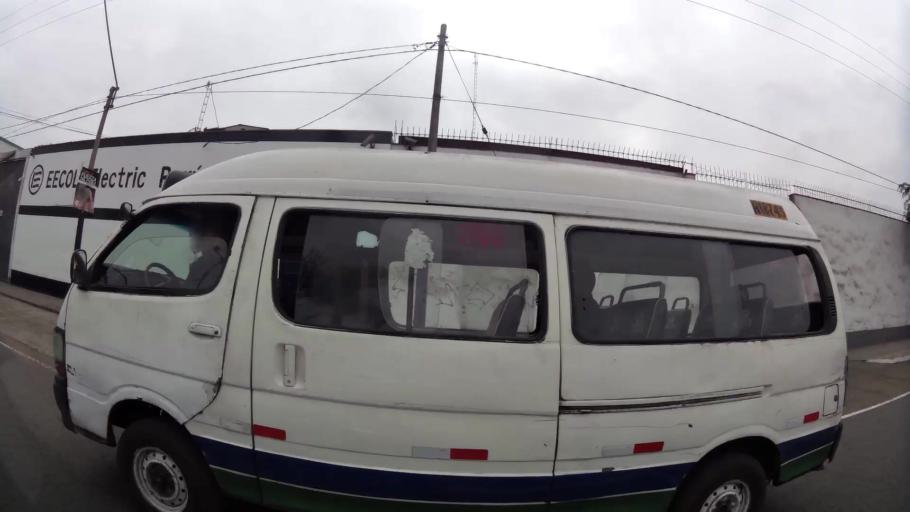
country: PE
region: Lima
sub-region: Lima
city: Surco
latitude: -12.1804
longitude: -76.9935
